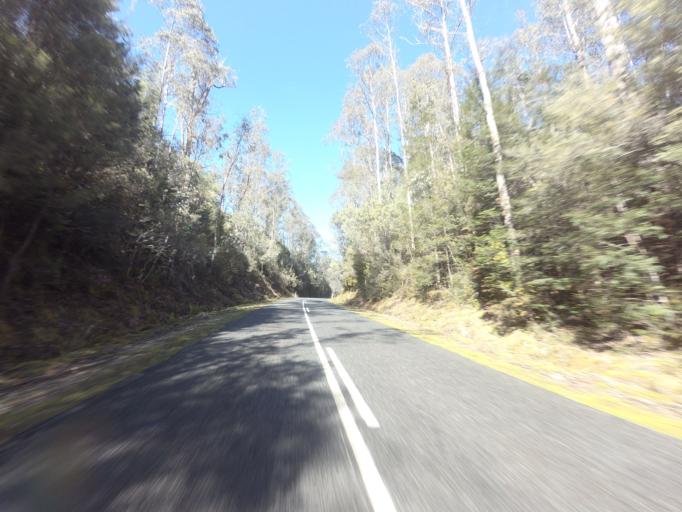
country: AU
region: Tasmania
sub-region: Derwent Valley
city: New Norfolk
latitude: -42.7367
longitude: 146.4234
